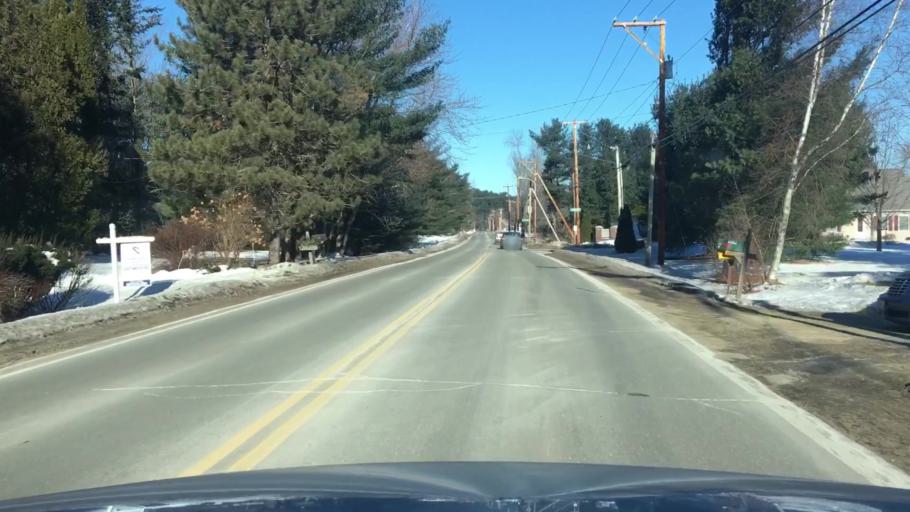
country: US
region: Maine
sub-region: Androscoggin County
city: Auburn
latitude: 44.0949
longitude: -70.2643
